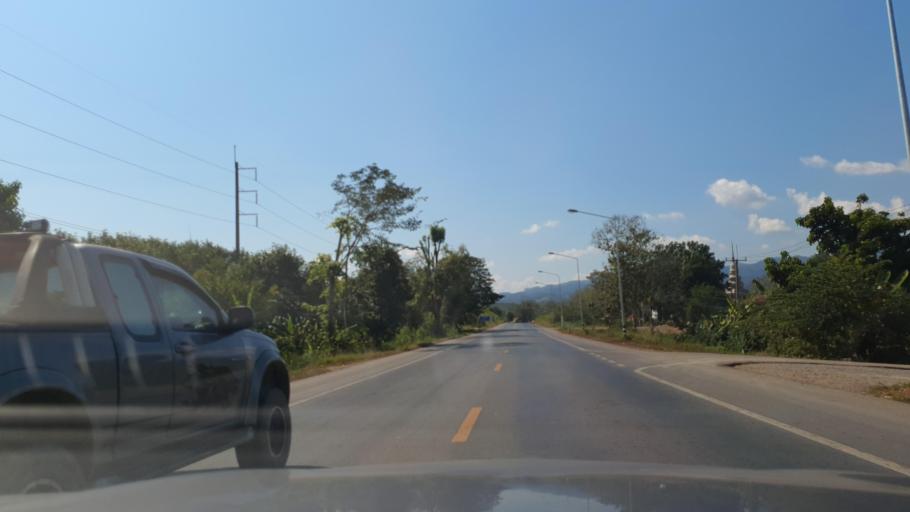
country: TH
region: Nan
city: Tha Wang Pha
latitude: 19.0187
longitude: 100.7873
